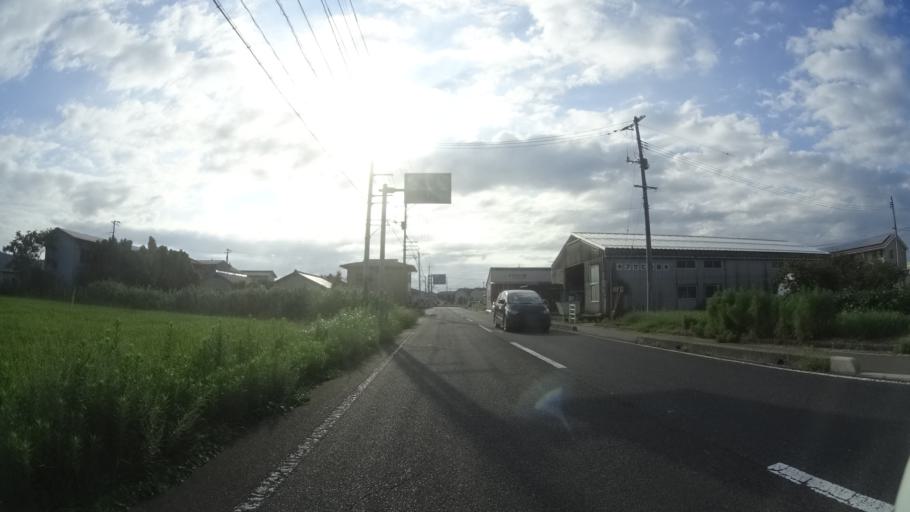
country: JP
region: Tottori
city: Kurayoshi
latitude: 35.4912
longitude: 133.8724
